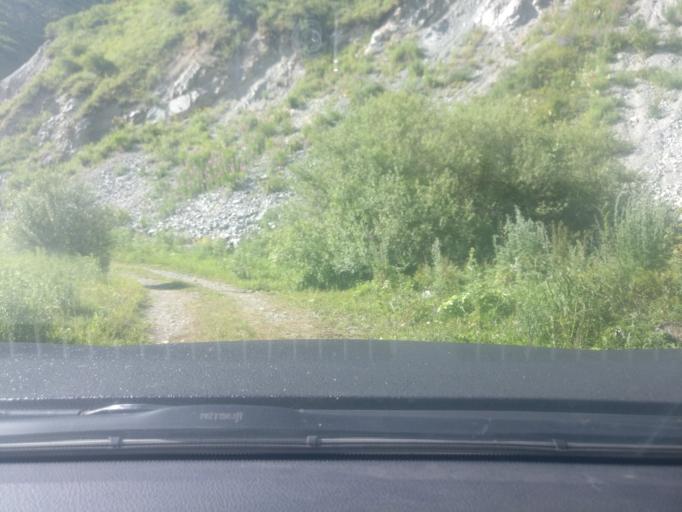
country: KZ
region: Almaty Qalasy
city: Almaty
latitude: 43.1075
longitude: 76.9544
